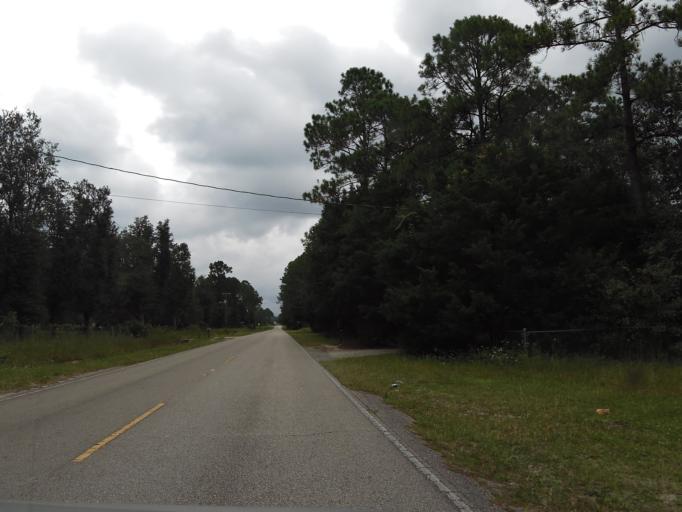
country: US
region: Florida
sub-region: Clay County
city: Middleburg
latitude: 30.1112
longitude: -81.9491
